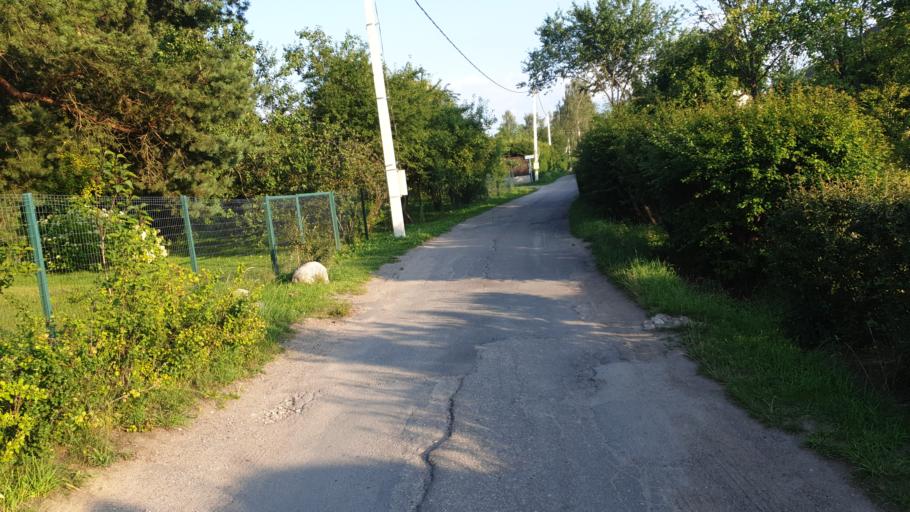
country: LT
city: Grigiskes
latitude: 54.7648
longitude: 25.0293
